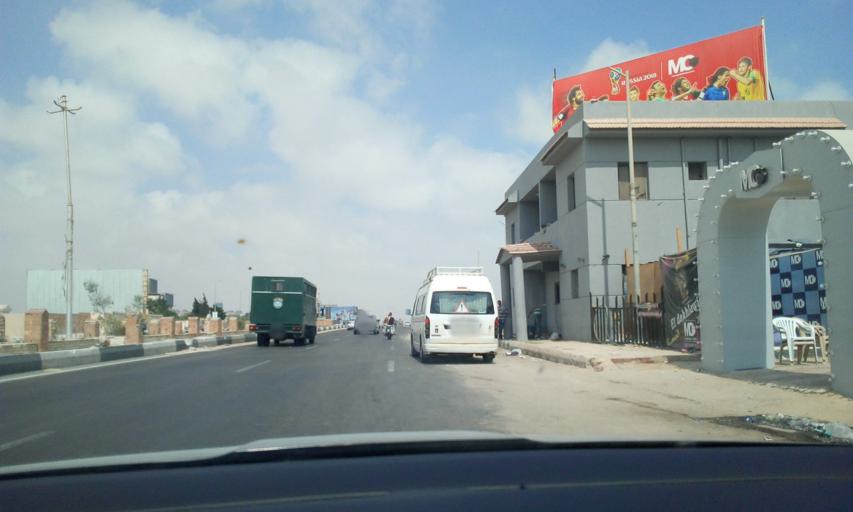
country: EG
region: Muhafazat Matruh
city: Al `Alamayn
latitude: 30.8354
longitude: 28.9599
